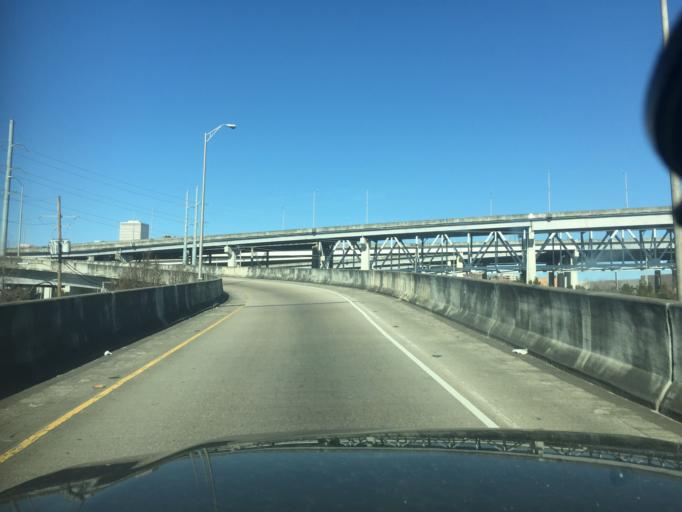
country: US
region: Louisiana
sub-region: Orleans Parish
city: New Orleans
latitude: 29.9364
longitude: -90.0662
